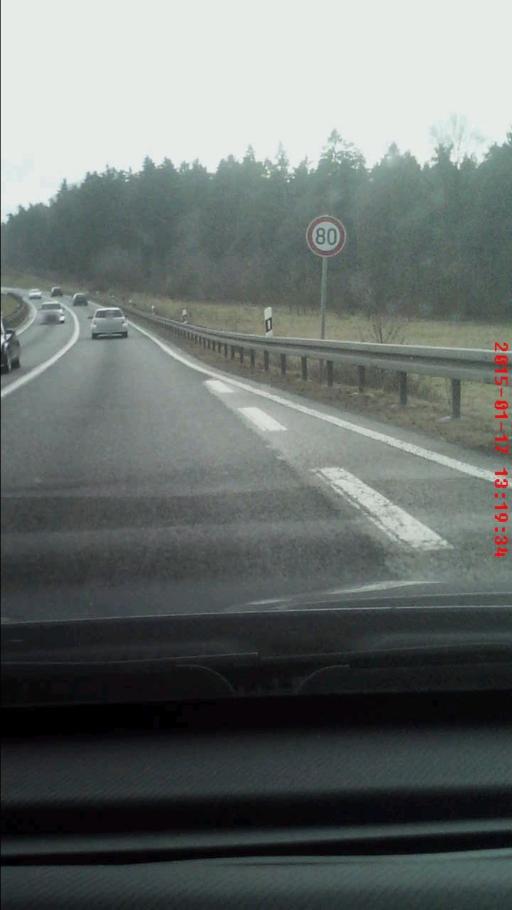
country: DE
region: Thuringia
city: Langewiesen
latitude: 50.7131
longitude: 10.9639
